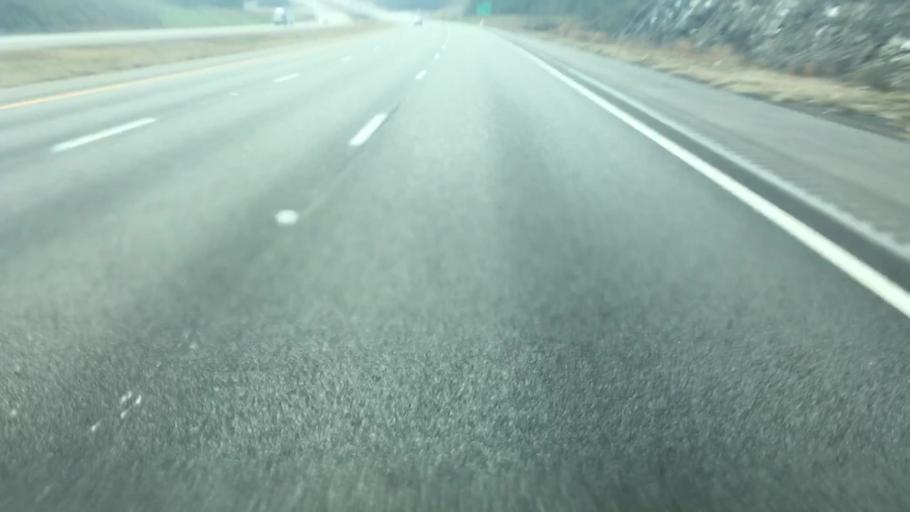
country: US
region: Alabama
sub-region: Walker County
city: Cordova
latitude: 33.7463
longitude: -87.2028
